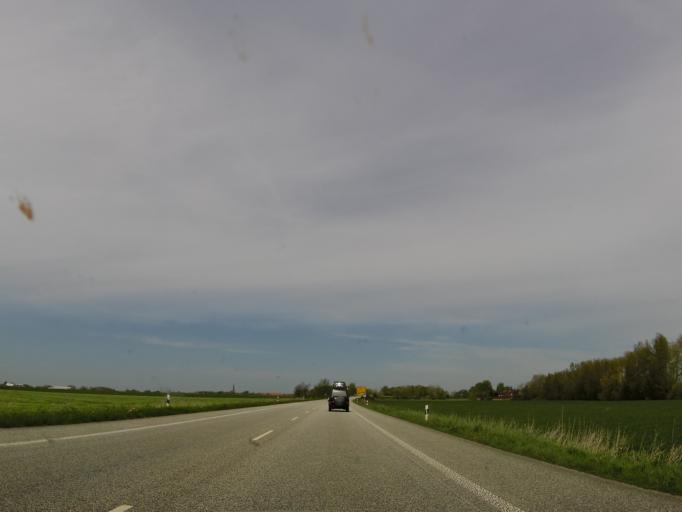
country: DE
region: Schleswig-Holstein
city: Karolinenkoog
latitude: 54.3028
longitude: 8.9635
